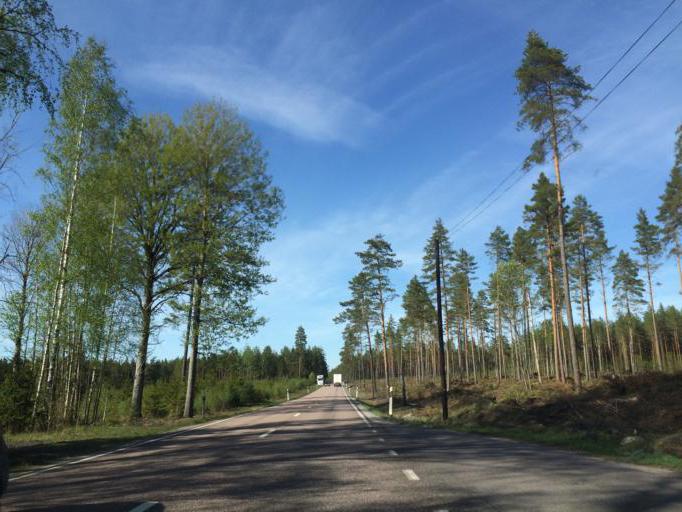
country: SE
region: Vaestmanland
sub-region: Kungsors Kommun
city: Kungsoer
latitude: 59.3124
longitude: 16.1080
